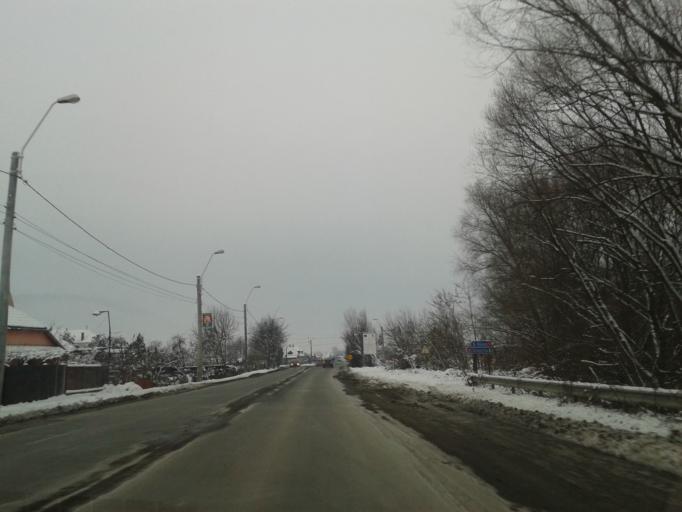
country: RO
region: Hunedoara
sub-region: Municipiul Deva
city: Cristur
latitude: 45.8538
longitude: 22.9554
